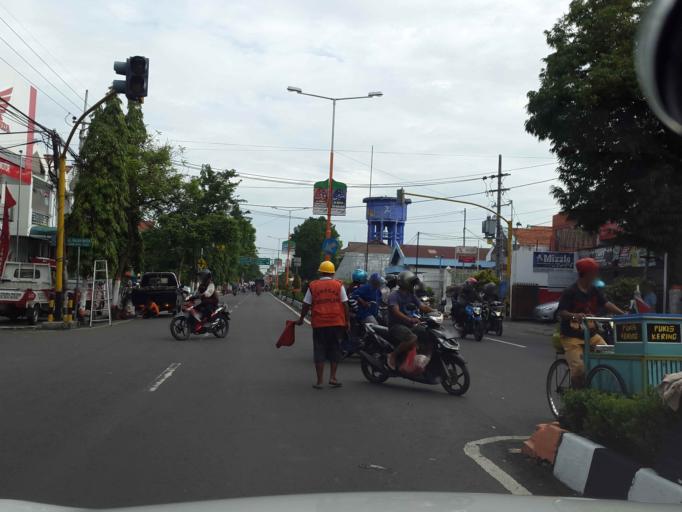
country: ID
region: East Java
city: Mojokerto
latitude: -7.4686
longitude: 112.4396
